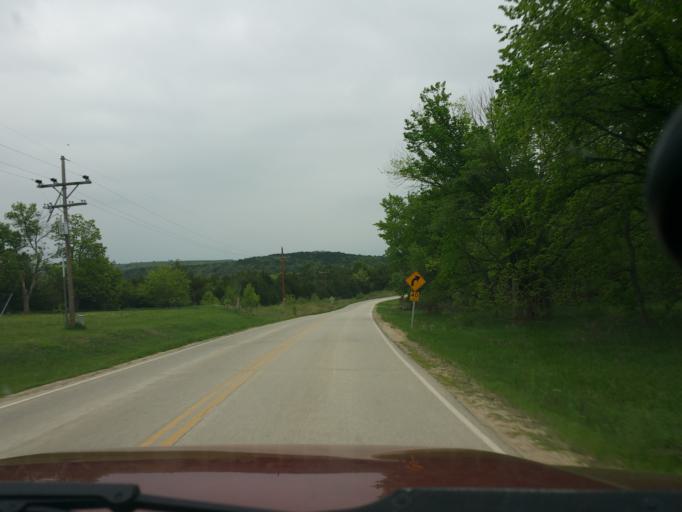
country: US
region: Kansas
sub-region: Riley County
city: Manhattan
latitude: 39.2654
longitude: -96.5723
